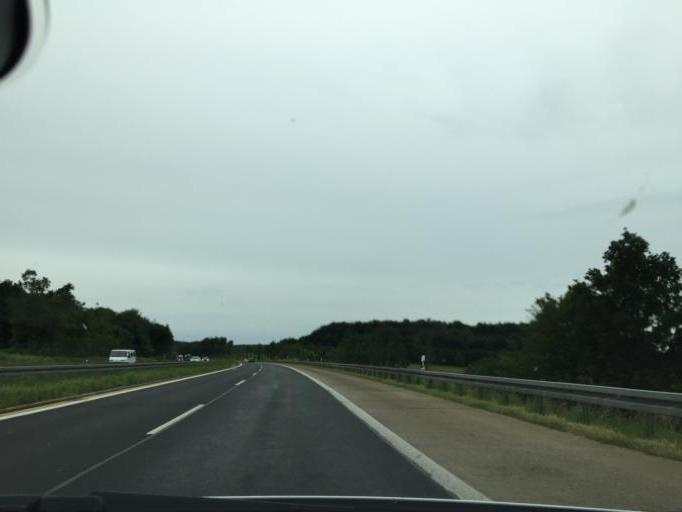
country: DE
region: Bavaria
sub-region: Regierungsbezirk Unterfranken
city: Schondra
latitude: 50.2848
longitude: 9.8569
